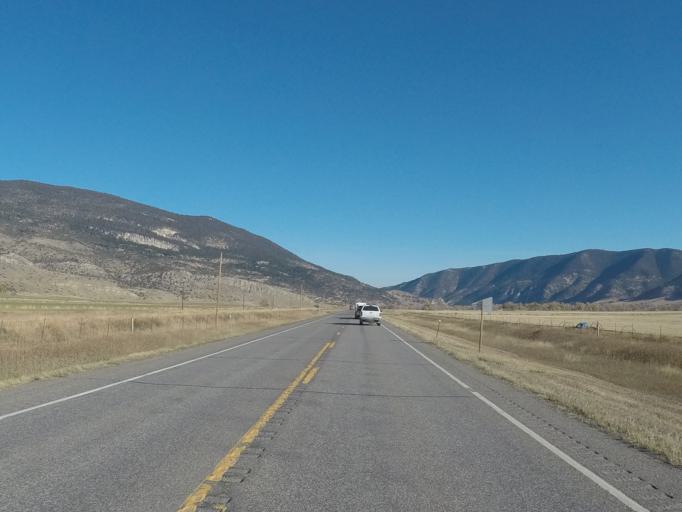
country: US
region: Montana
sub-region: Park County
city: Livingston
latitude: 45.5526
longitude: -110.5965
